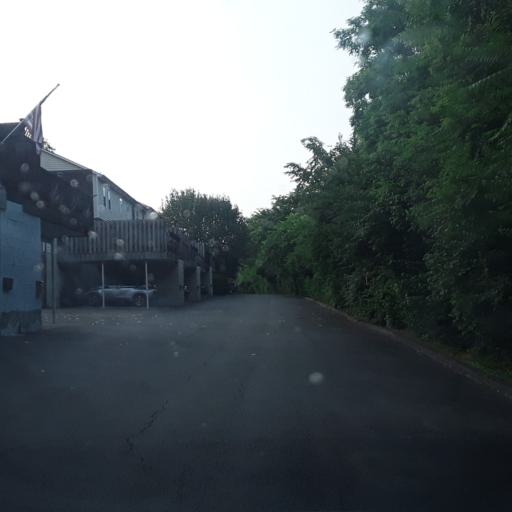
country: US
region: Tennessee
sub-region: Williamson County
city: Brentwood Estates
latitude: 36.0496
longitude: -86.7285
